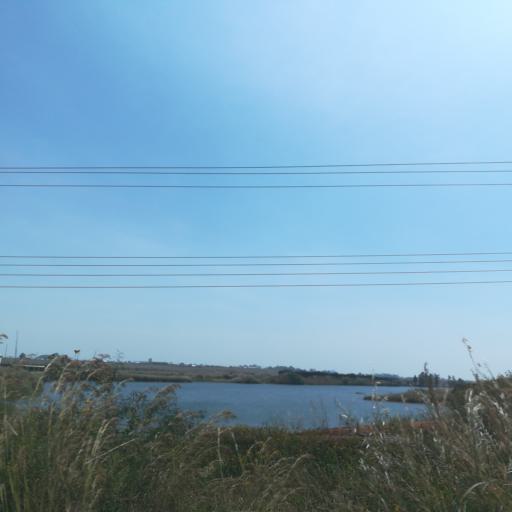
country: NG
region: Plateau
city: Bukuru
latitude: 9.8467
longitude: 8.9155
